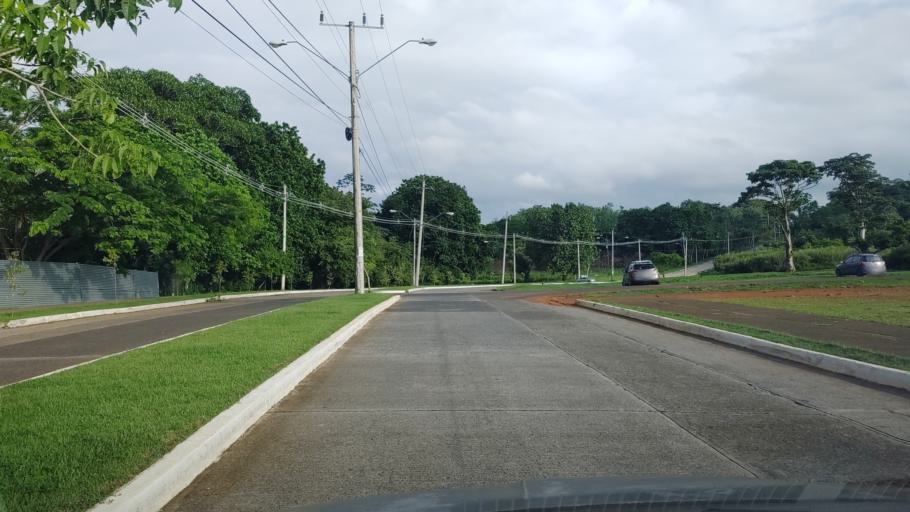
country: PA
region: Panama
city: Nuevo Arraijan
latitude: 8.9197
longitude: -79.7489
